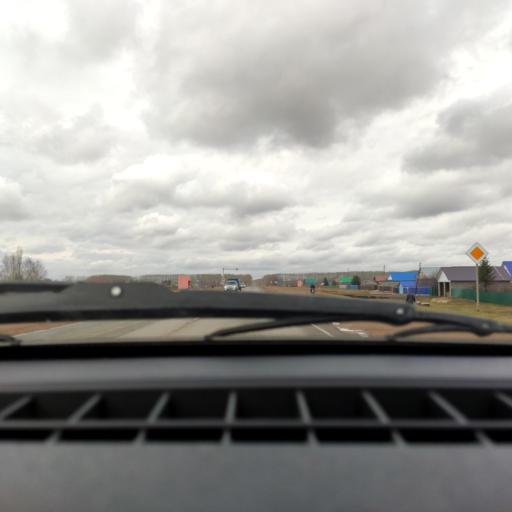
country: RU
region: Bashkortostan
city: Asanovo
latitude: 54.9621
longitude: 55.5481
